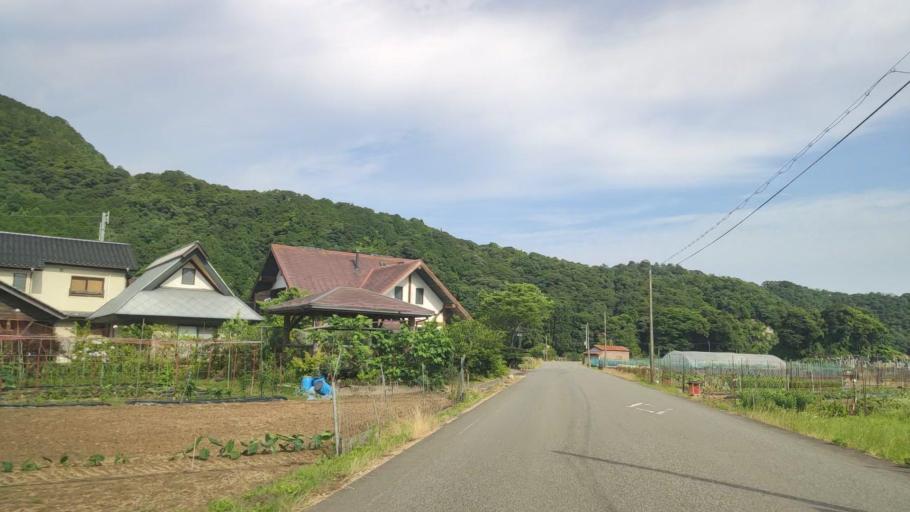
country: JP
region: Hyogo
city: Toyooka
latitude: 35.6336
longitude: 134.8387
